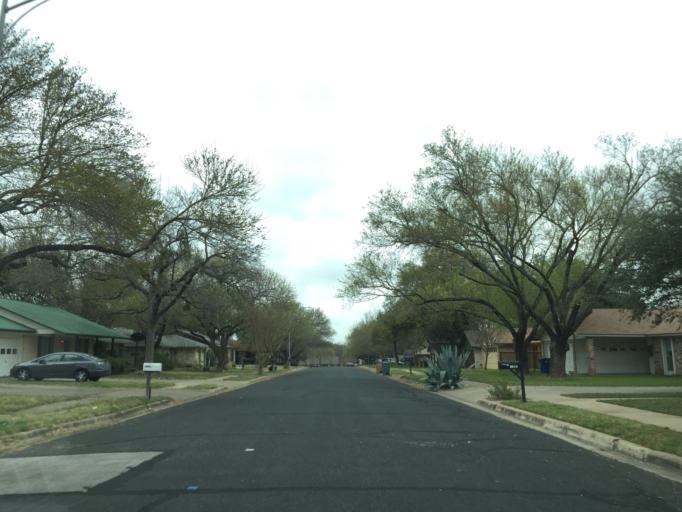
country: US
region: Texas
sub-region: Williamson County
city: Jollyville
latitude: 30.4133
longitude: -97.7417
